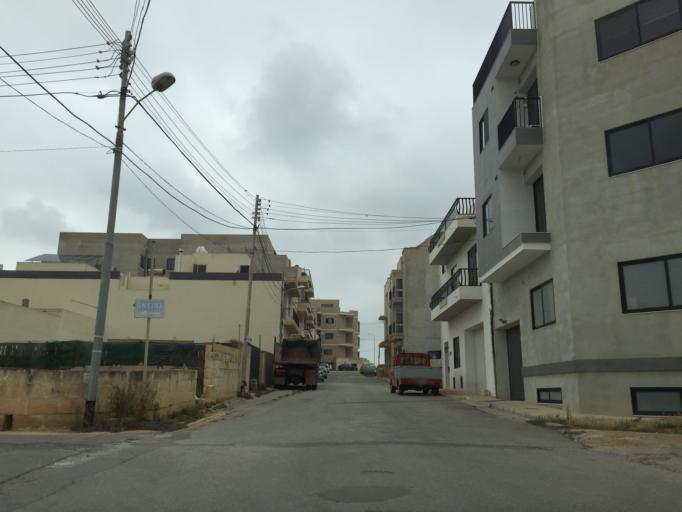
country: MT
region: L-Imgarr
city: Imgarr
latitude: 35.9216
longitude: 14.3684
